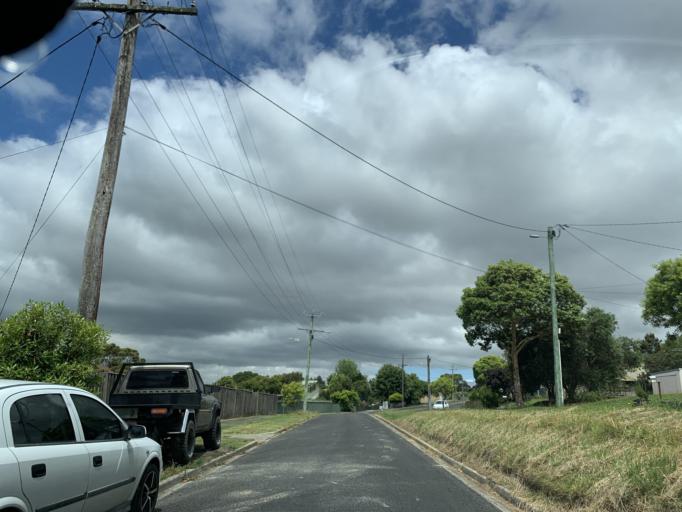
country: AU
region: Victoria
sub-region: Latrobe
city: Morwell
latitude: -38.1591
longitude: 146.3636
